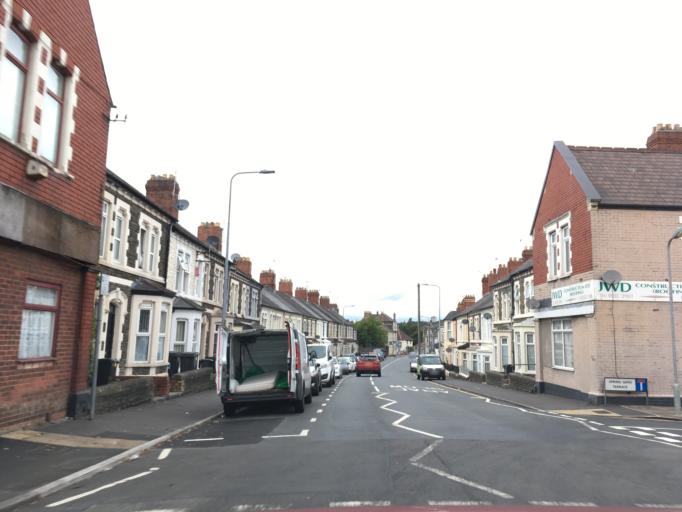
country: GB
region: Wales
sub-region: Cardiff
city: Cardiff
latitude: 51.4896
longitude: -3.1488
